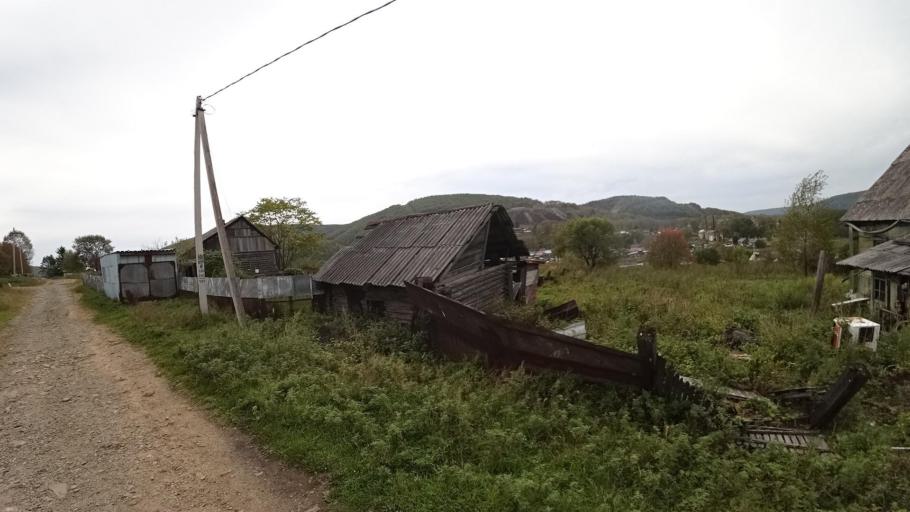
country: RU
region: Jewish Autonomous Oblast
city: Khingansk
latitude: 49.1294
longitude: 131.2019
